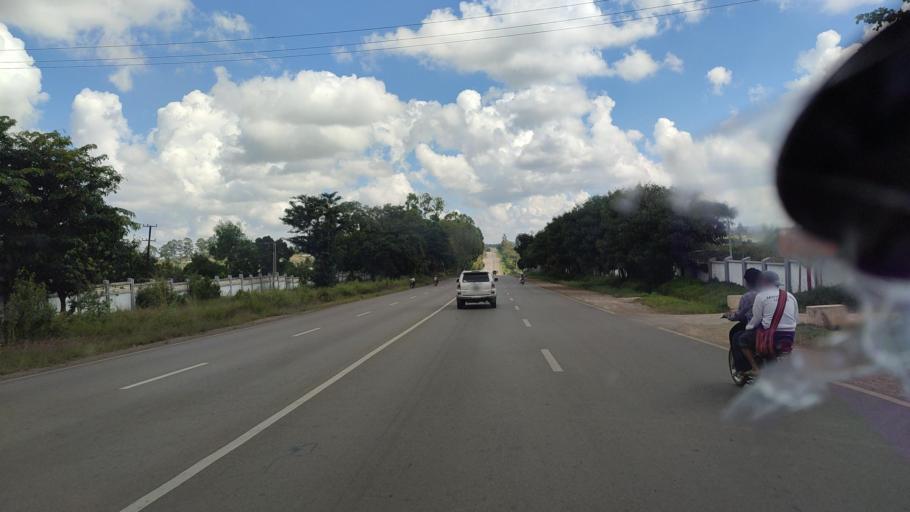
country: MM
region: Shan
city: Taunggyi
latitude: 20.6656
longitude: 96.6490
